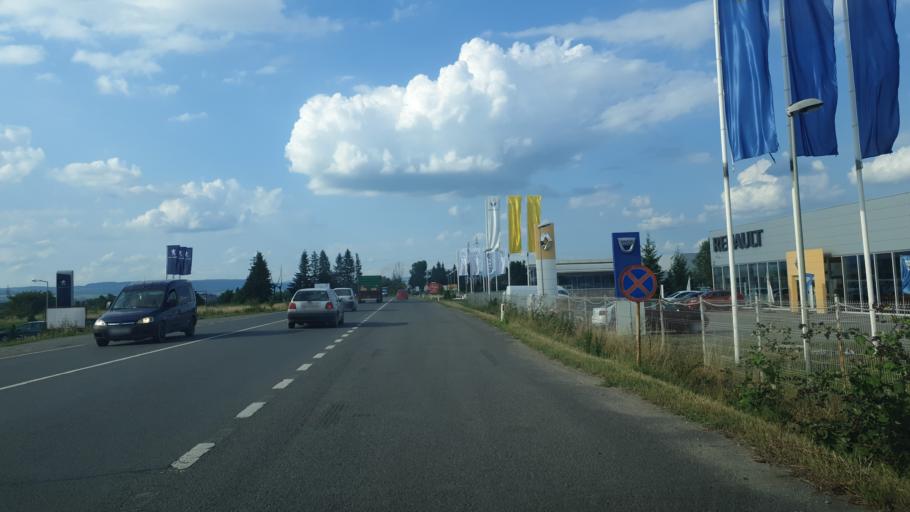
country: RO
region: Covasna
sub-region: Municipiul Sfantu Gheorghe
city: Sfantu-Gheorghe
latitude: 45.8433
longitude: 25.8038
